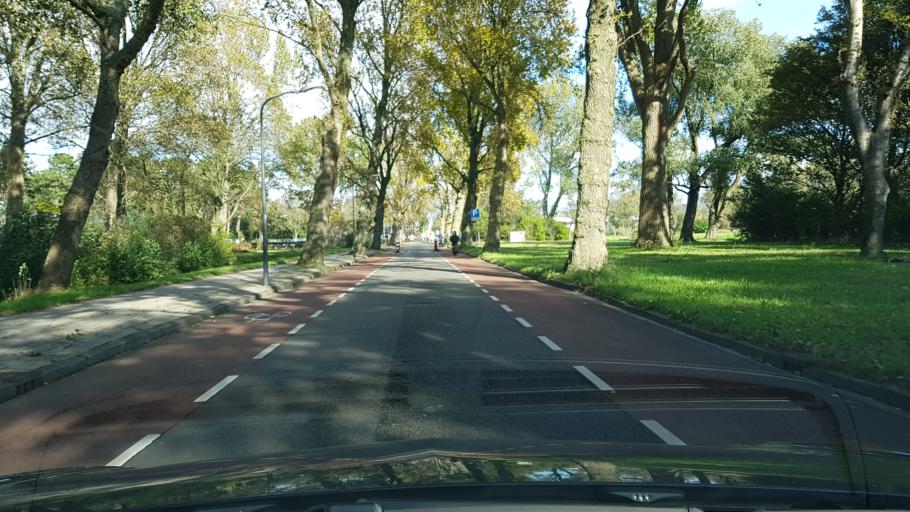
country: NL
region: North Holland
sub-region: Gemeente Velsen
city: Velsen-Zuid
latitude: 52.4208
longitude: 4.6582
